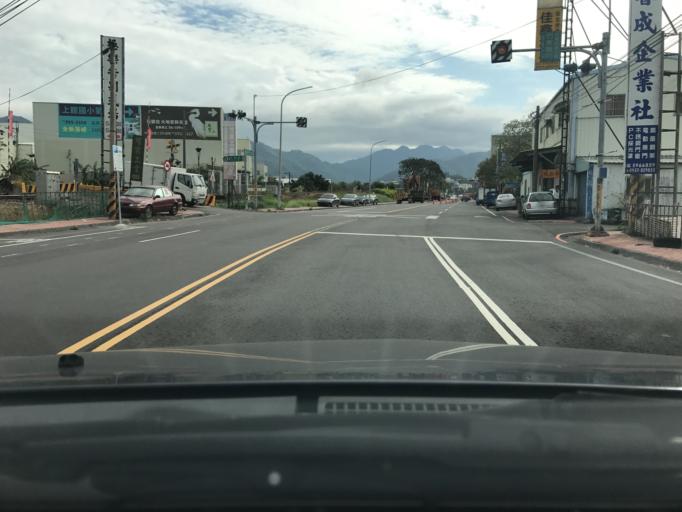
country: TW
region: Taiwan
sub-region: Hsinchu
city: Zhubei
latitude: 24.7320
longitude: 121.1000
